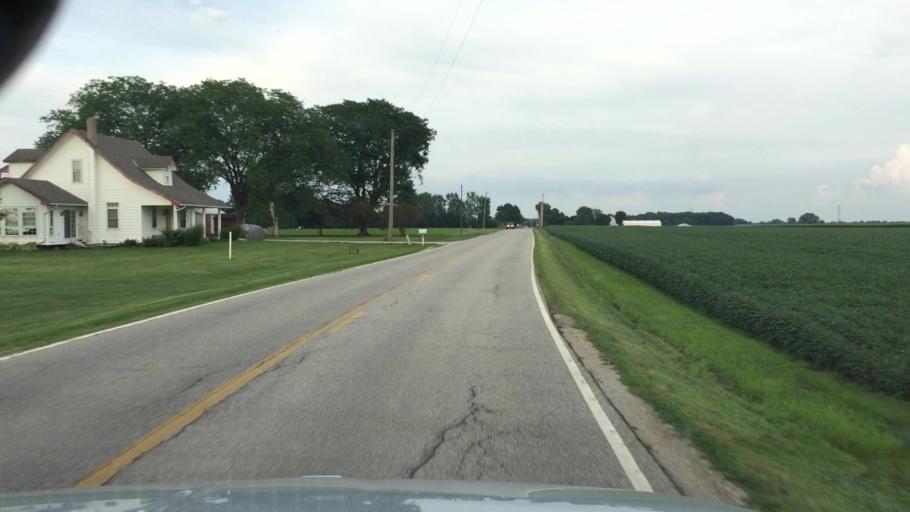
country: US
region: Ohio
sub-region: Madison County
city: Plain City
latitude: 40.0753
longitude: -83.2186
